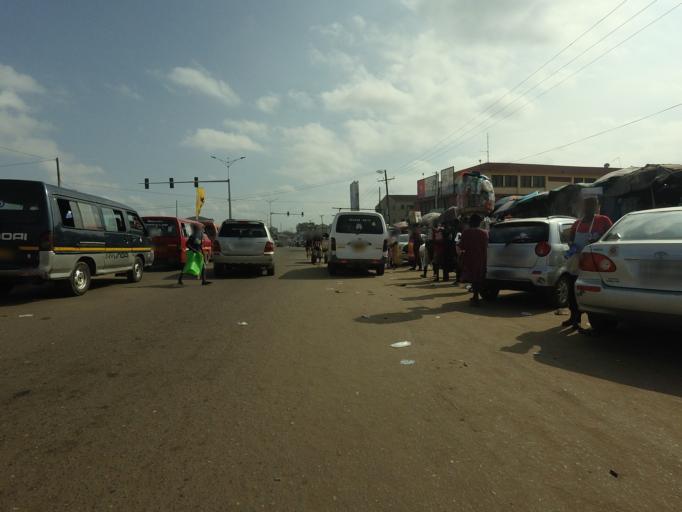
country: GH
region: Greater Accra
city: Tema
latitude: 5.6884
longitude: -0.0298
